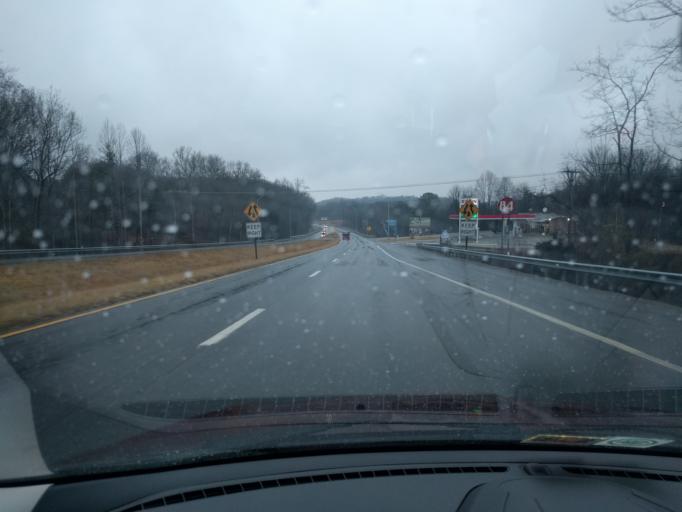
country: US
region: Virginia
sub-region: Pulaski County
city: Pulaski
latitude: 37.0298
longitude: -80.7319
